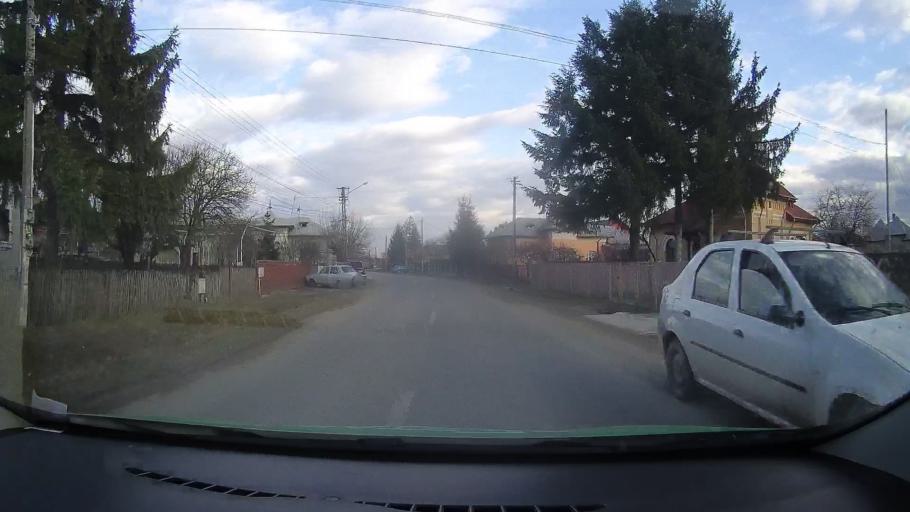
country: RO
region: Dambovita
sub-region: Comuna Gura Ocnitei
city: Gura Ocnitei
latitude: 44.9397
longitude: 25.5698
